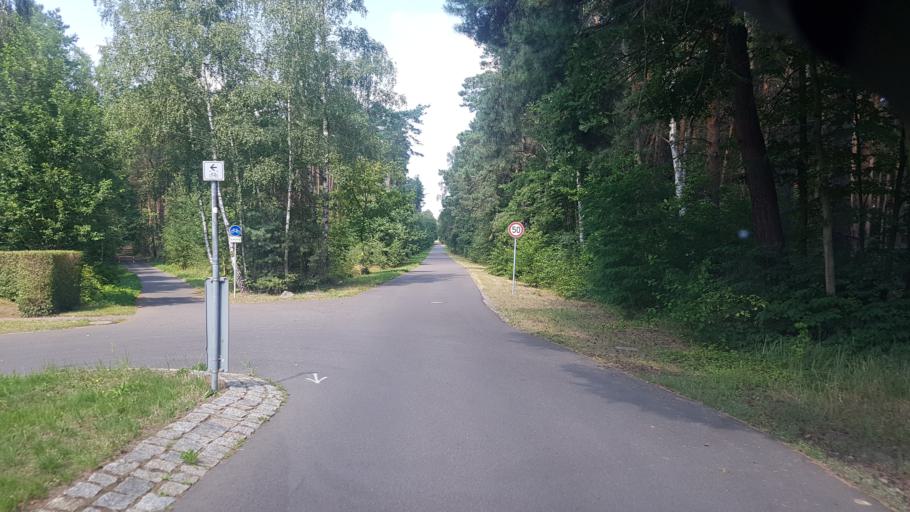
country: DE
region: Brandenburg
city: Spremberg
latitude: 51.6119
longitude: 14.3998
